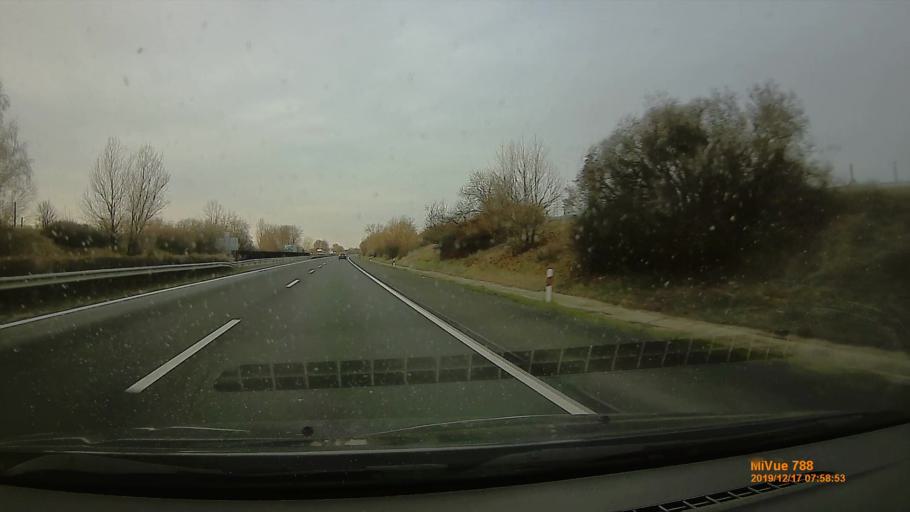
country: HU
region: Somogy
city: Siofok
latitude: 46.8913
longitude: 18.0438
